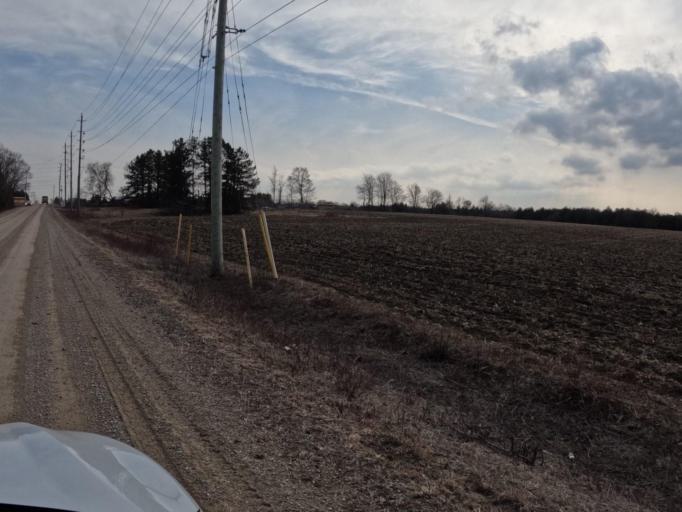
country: CA
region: Ontario
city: Shelburne
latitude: 43.9067
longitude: -80.3028
